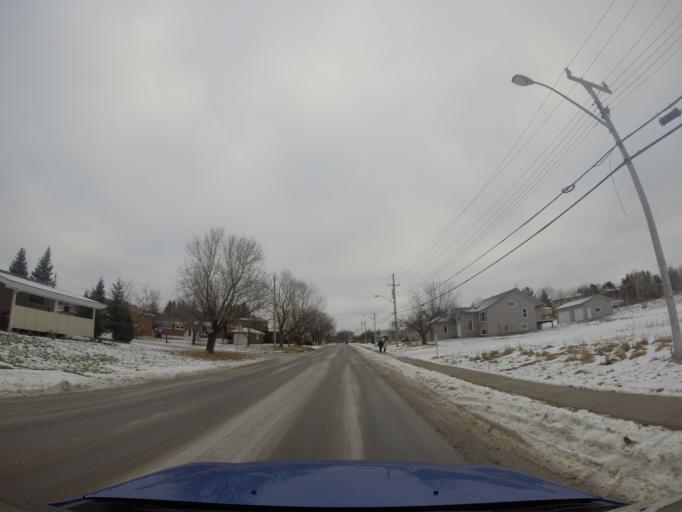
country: CA
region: Ontario
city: Greater Sudbury
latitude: 46.4621
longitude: -81.0231
